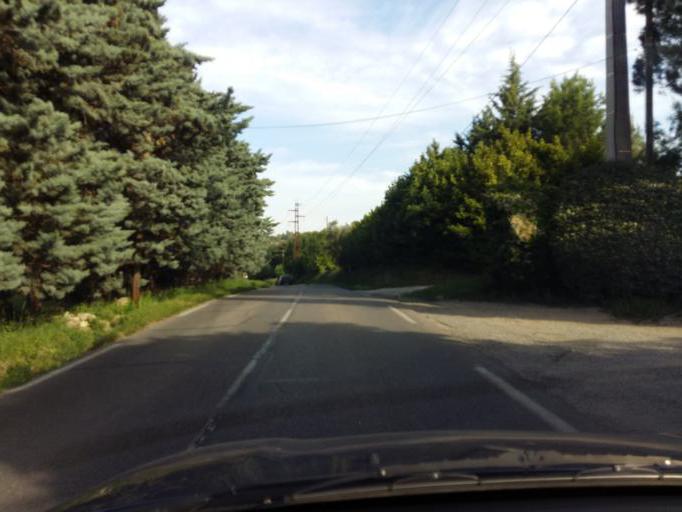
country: FR
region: Provence-Alpes-Cote d'Azur
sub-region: Departement des Bouches-du-Rhone
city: Pelissanne
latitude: 43.6347
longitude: 5.1294
